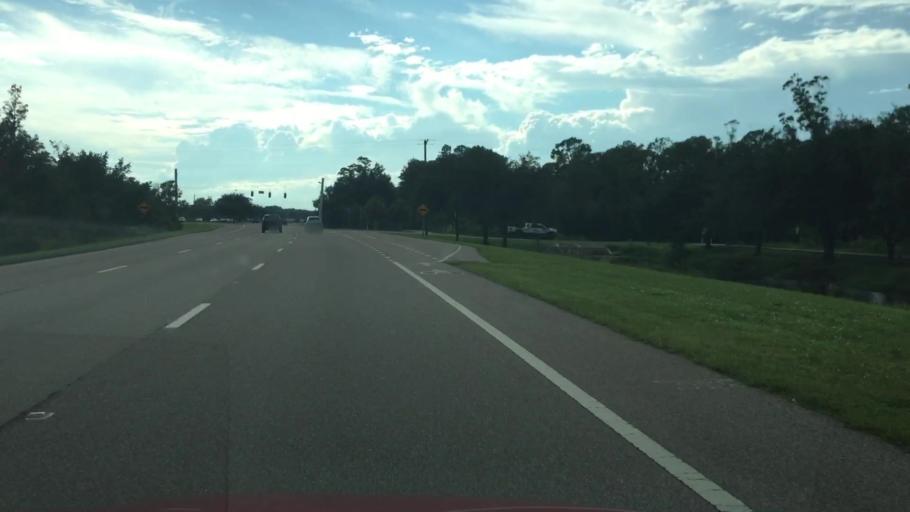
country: US
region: Florida
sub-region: Lee County
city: Villas
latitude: 26.5475
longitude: -81.8145
